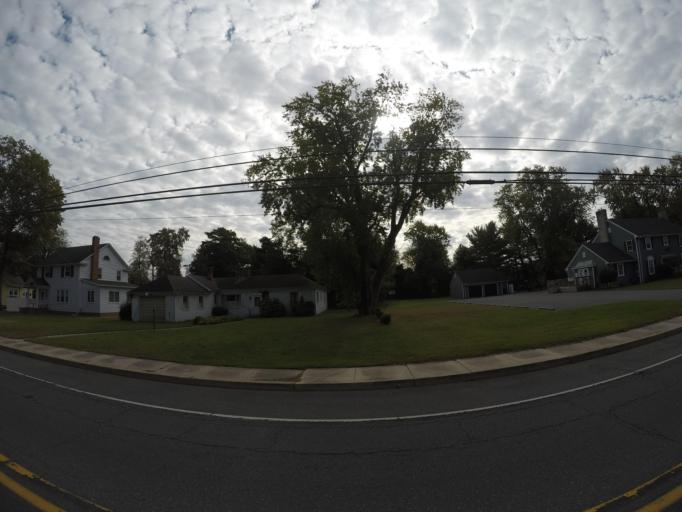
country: US
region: Delaware
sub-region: Sussex County
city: Georgetown
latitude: 38.6879
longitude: -75.3889
